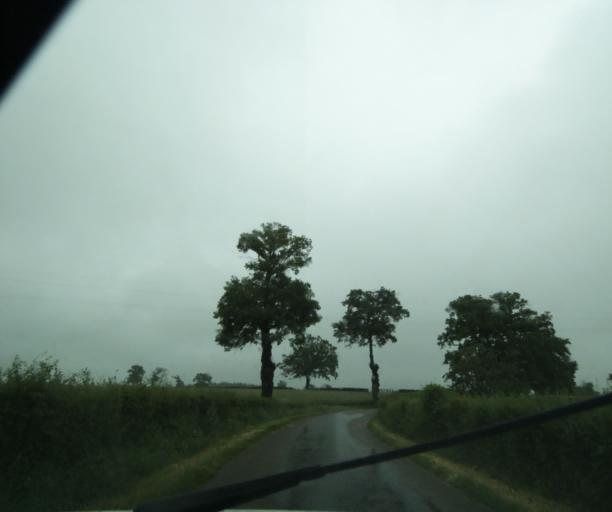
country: FR
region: Bourgogne
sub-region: Departement de Saone-et-Loire
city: Charolles
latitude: 46.4187
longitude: 4.2818
